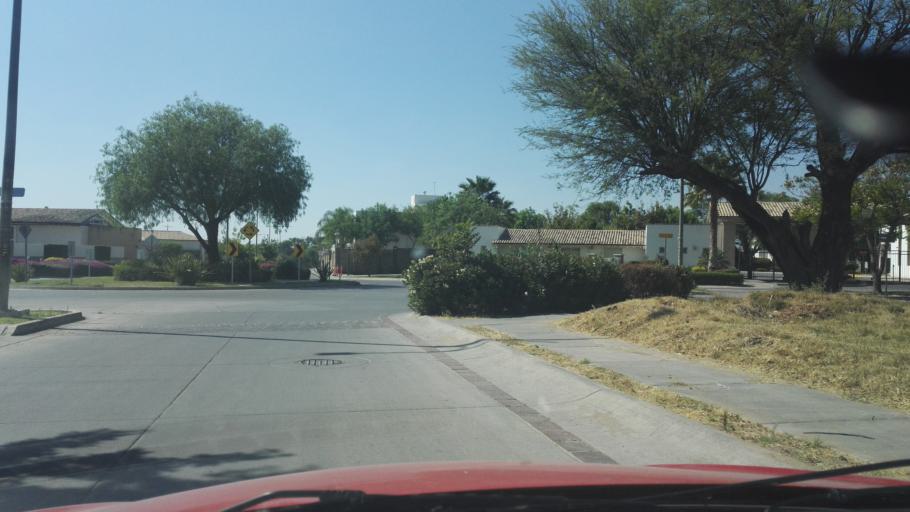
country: MX
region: Guanajuato
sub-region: Leon
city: Medina
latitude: 21.1264
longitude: -101.6109
